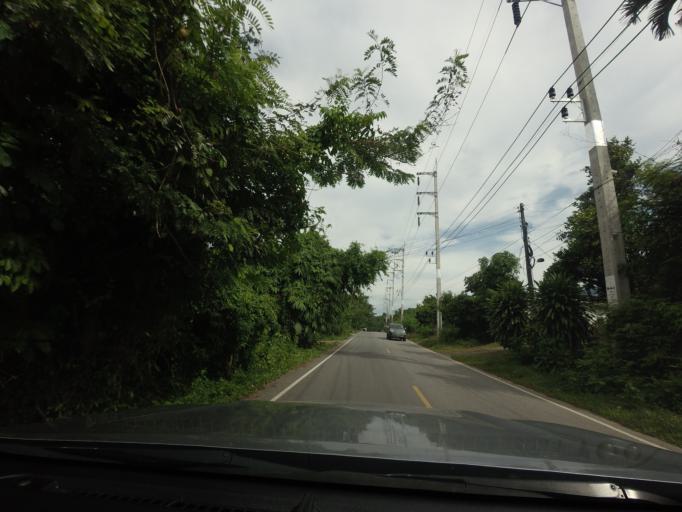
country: TH
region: Yala
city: Yala
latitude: 6.5086
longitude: 101.2884
